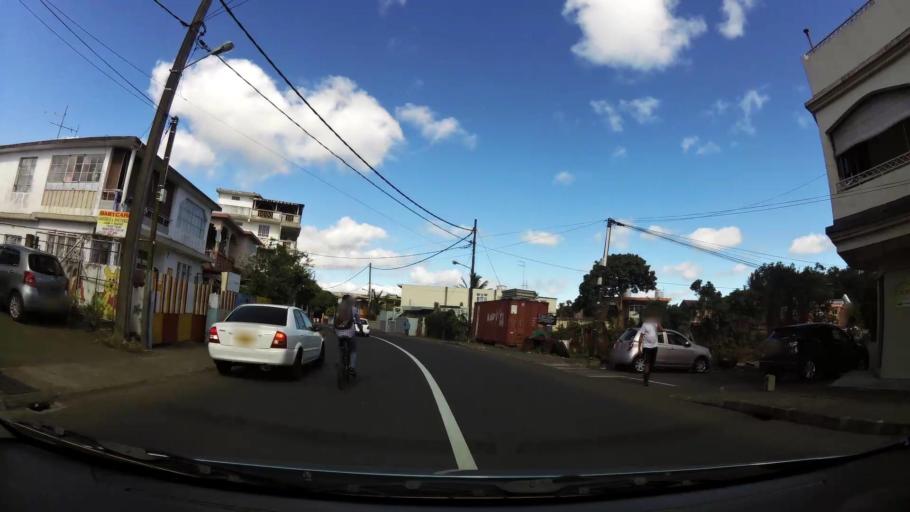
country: MU
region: Plaines Wilhems
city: Vacoas
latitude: -20.3093
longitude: 57.4898
